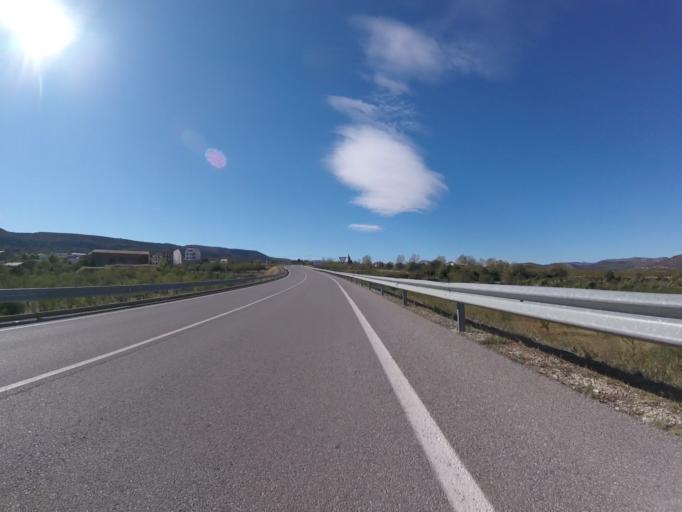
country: ES
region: Valencia
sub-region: Provincia de Castello
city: Albocasser
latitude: 40.3597
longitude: 0.0194
